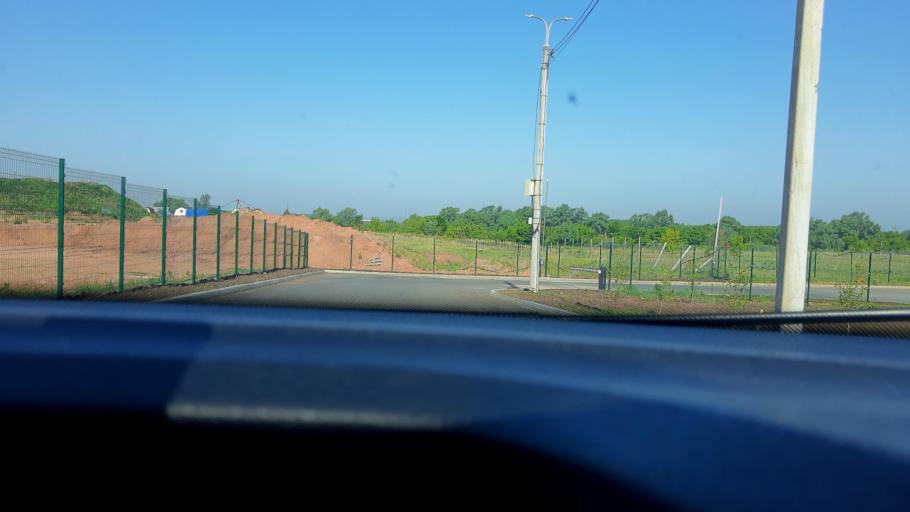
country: RU
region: Bashkortostan
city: Ufa
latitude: 54.6018
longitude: 55.9020
